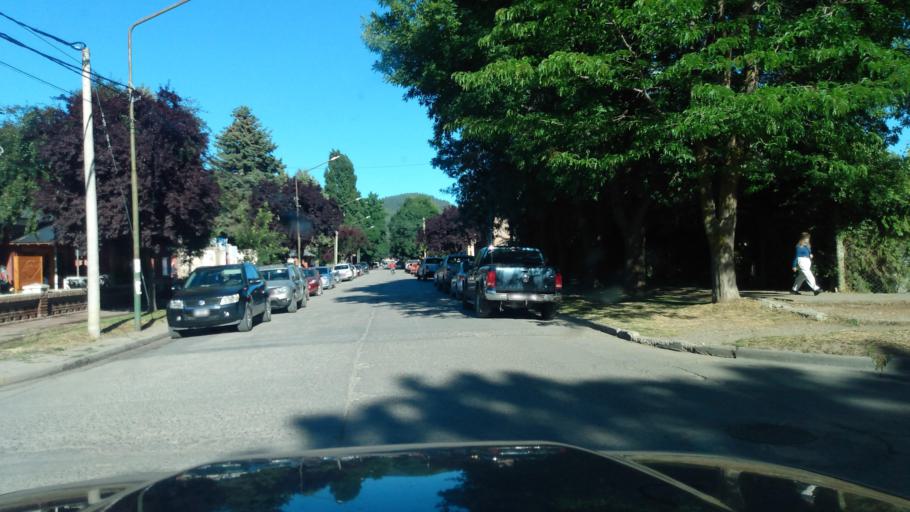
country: AR
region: Neuquen
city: Junin de los Andes
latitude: -39.9526
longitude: -71.0707
